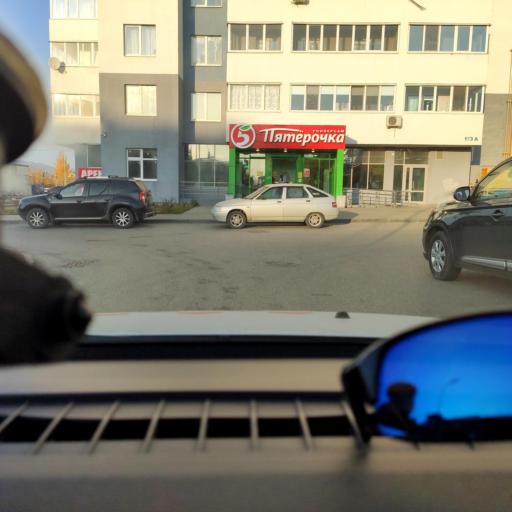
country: RU
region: Samara
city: Samara
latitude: 53.2660
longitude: 50.2312
